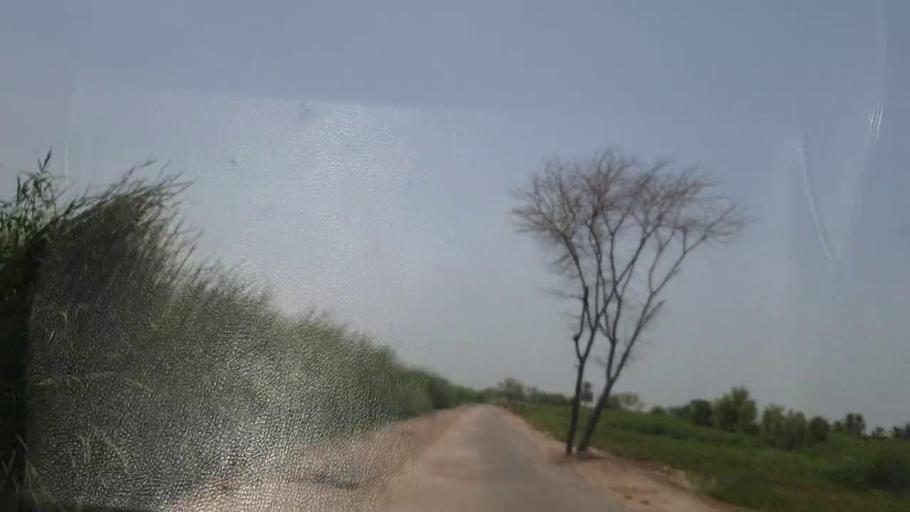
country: PK
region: Sindh
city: Bozdar
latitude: 27.2495
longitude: 68.6584
